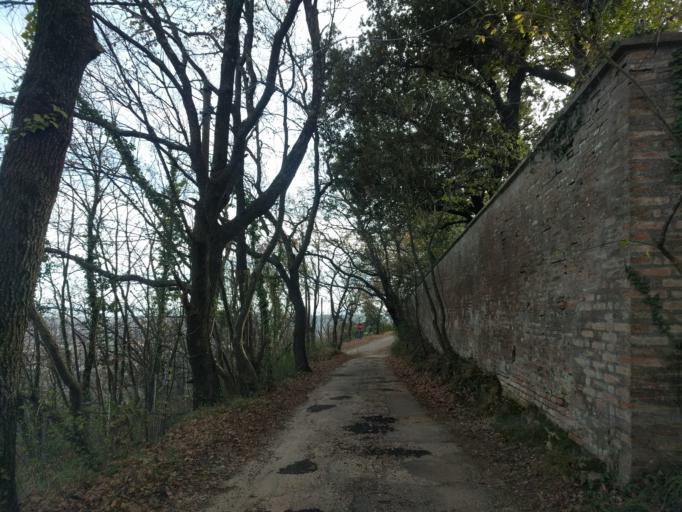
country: IT
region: The Marches
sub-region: Provincia di Pesaro e Urbino
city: Centinarola
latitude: 43.8195
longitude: 12.9746
